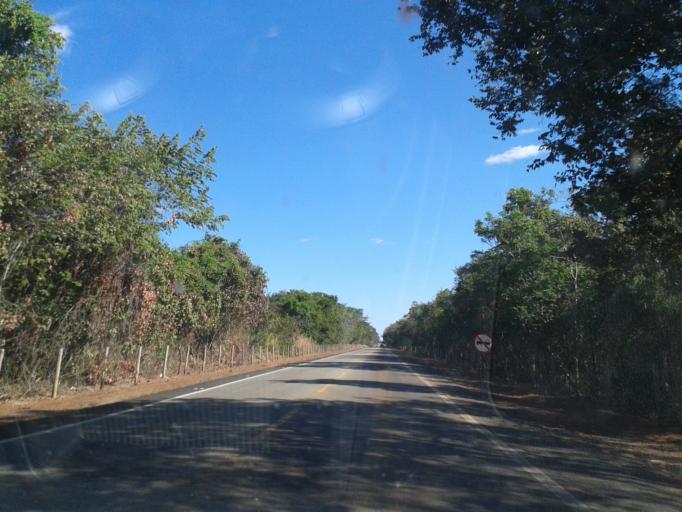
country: BR
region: Goias
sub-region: Mozarlandia
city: Mozarlandia
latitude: -14.6677
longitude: -50.5331
